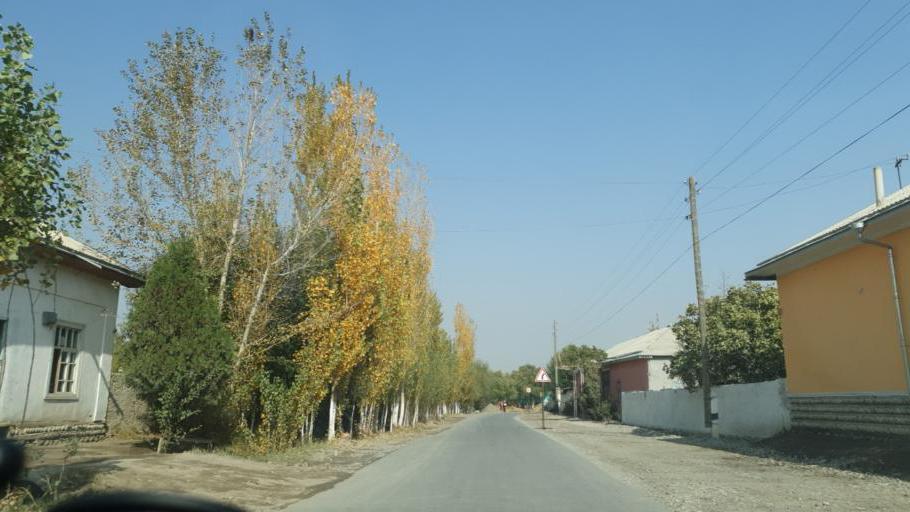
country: UZ
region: Fergana
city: Beshariq
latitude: 40.4938
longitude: 70.6213
